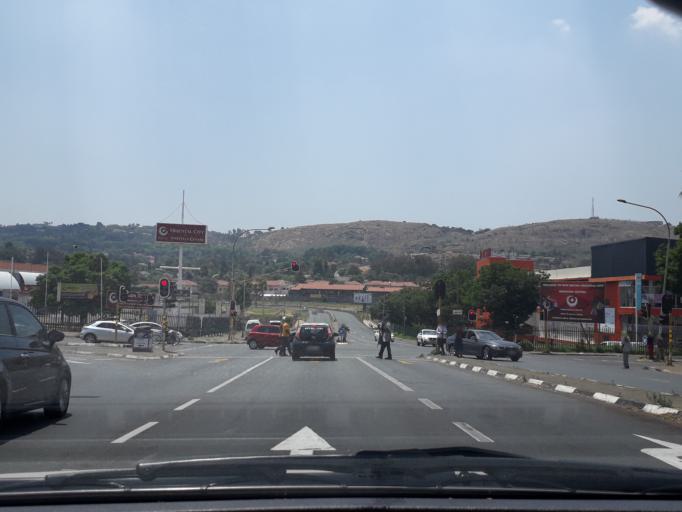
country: ZA
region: Gauteng
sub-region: City of Johannesburg Metropolitan Municipality
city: Johannesburg
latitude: -26.1801
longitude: 28.1100
